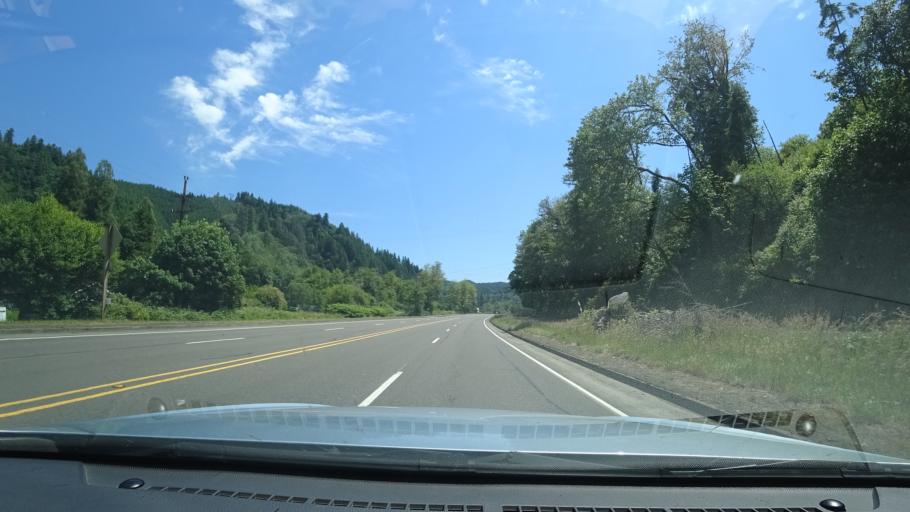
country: US
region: Oregon
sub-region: Lane County
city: Florence
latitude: 44.0295
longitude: -123.8585
